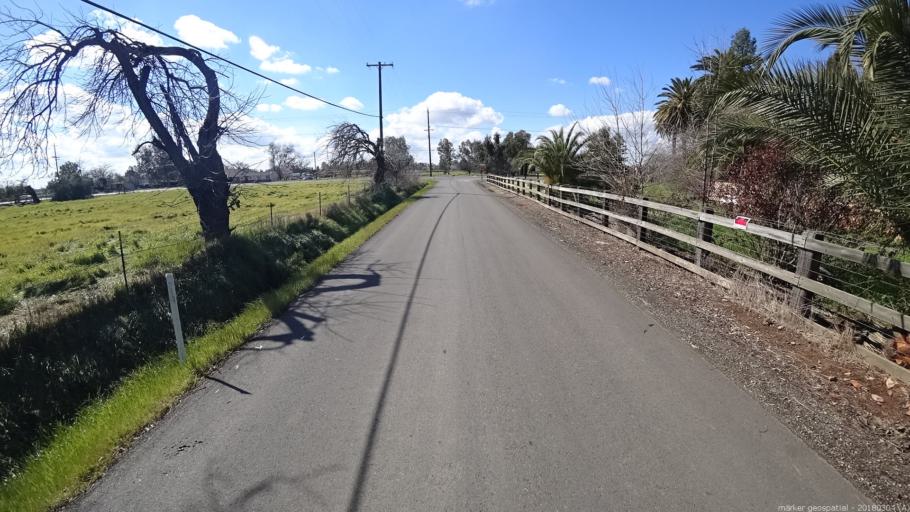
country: US
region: California
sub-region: Sacramento County
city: Vineyard
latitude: 38.4726
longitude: -121.3339
